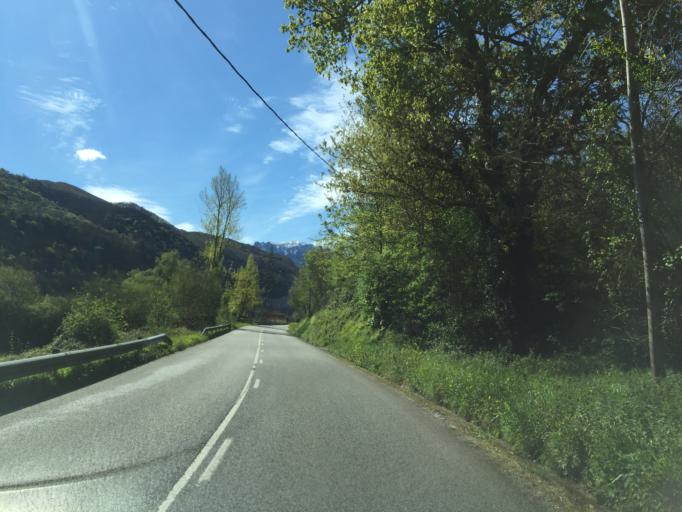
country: ES
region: Asturias
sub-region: Province of Asturias
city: Proaza
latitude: 43.3204
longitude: -5.9929
